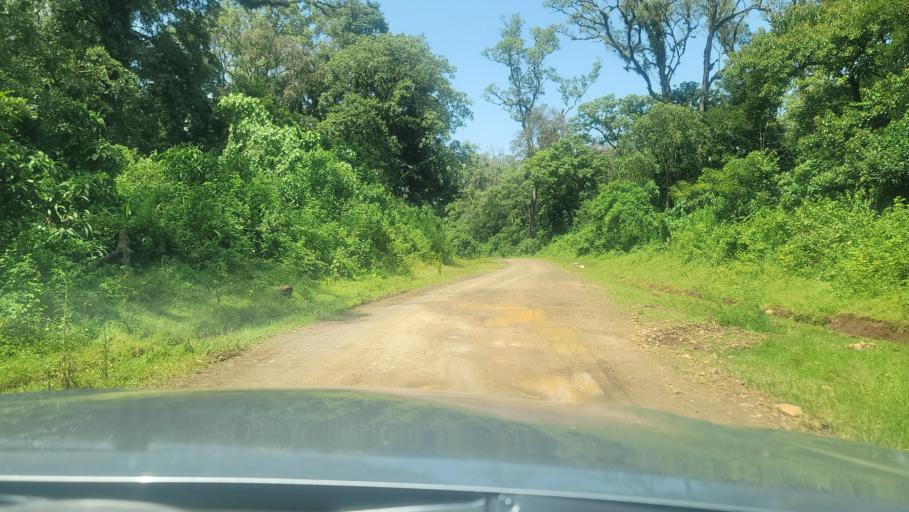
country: ET
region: Southern Nations, Nationalities, and People's Region
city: Bonga
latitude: 7.6537
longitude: 36.2466
